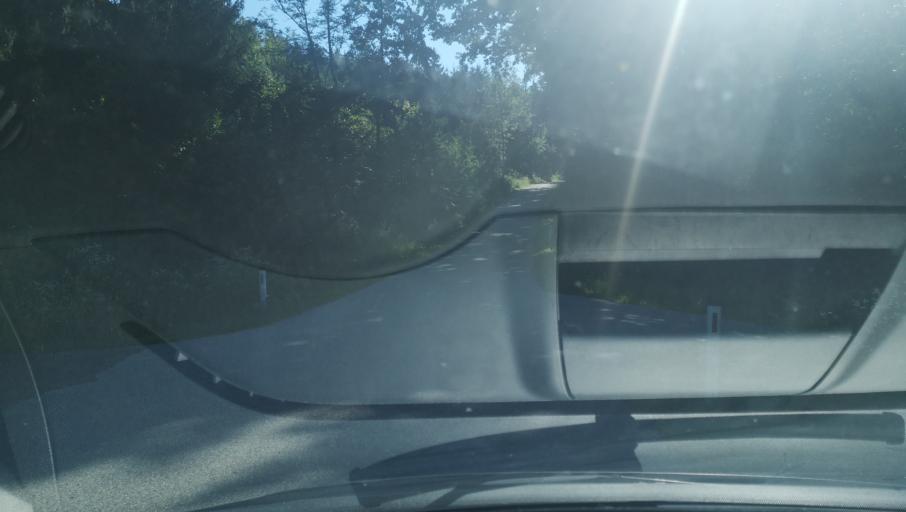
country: AT
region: Lower Austria
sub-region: Politischer Bezirk Melk
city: Blindenmarkt
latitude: 48.1349
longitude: 14.9963
